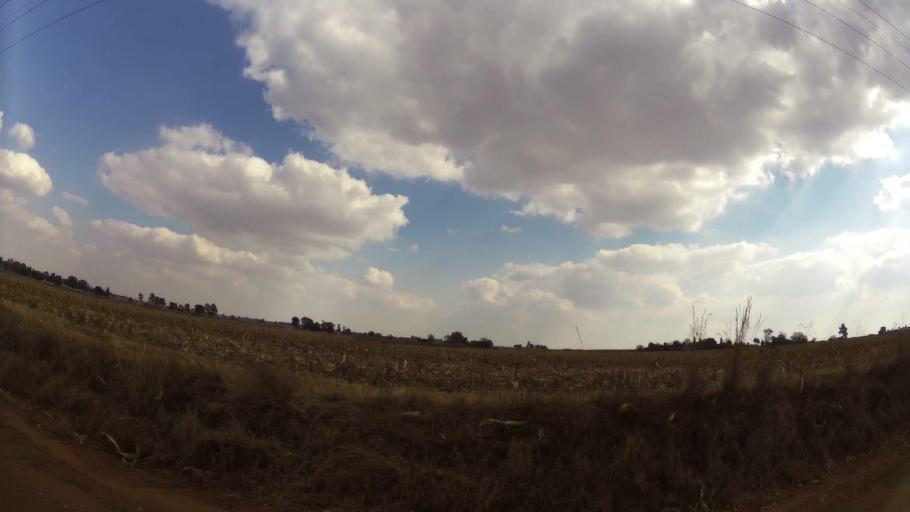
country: ZA
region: Mpumalanga
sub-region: Nkangala District Municipality
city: Delmas
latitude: -26.1353
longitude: 28.6700
